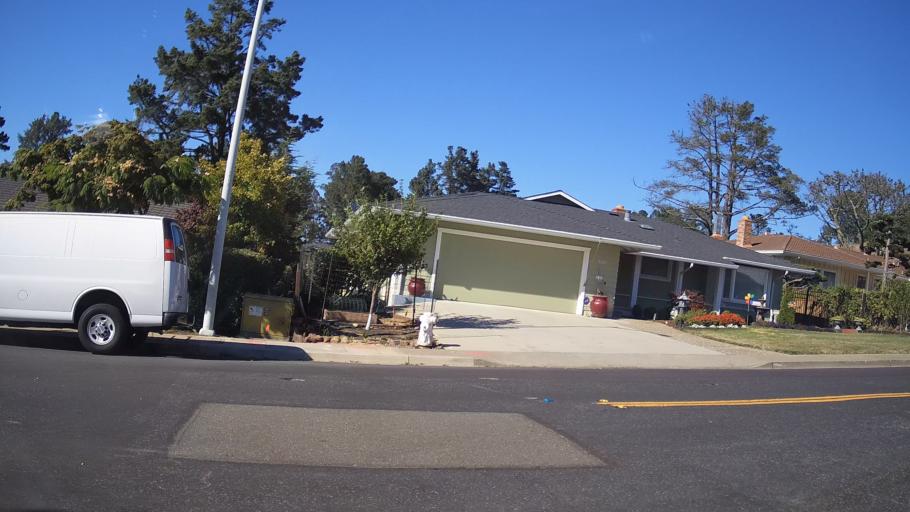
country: US
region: California
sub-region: Contra Costa County
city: East Richmond Heights
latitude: 37.9323
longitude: -122.3068
